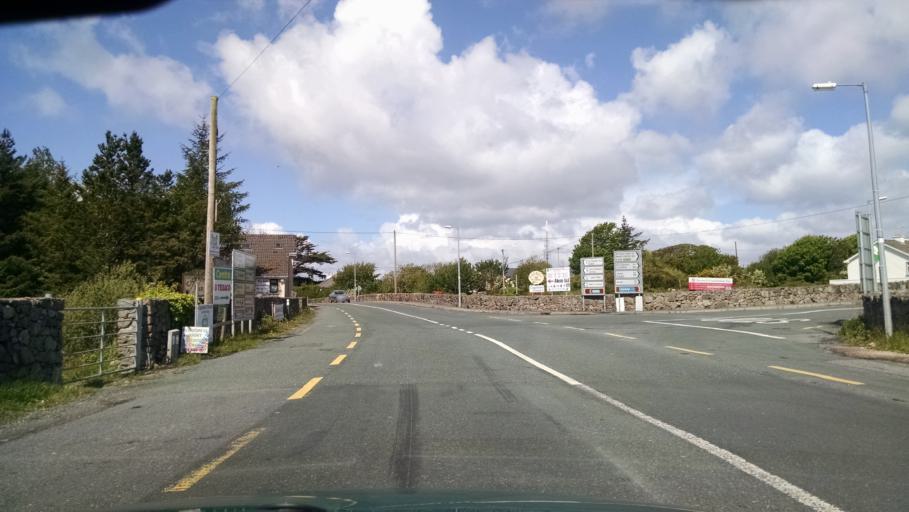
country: IE
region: Connaught
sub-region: County Galway
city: Oughterard
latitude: 53.2877
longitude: -9.5483
